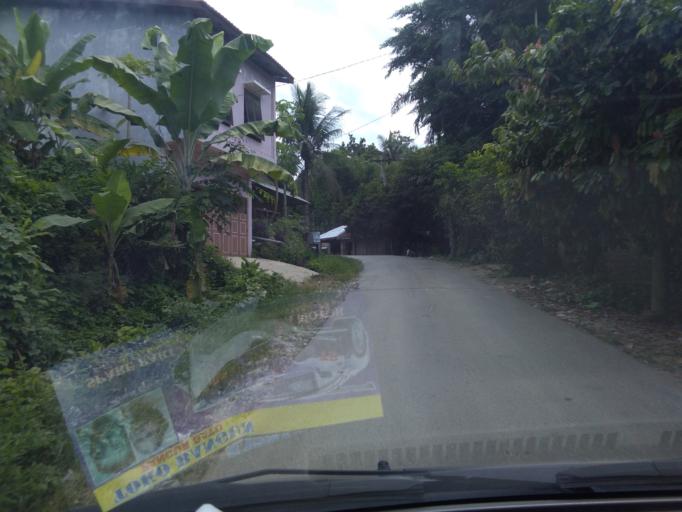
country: ID
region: North Sumatra
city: Deli Tua
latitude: 3.3052
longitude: 98.8087
